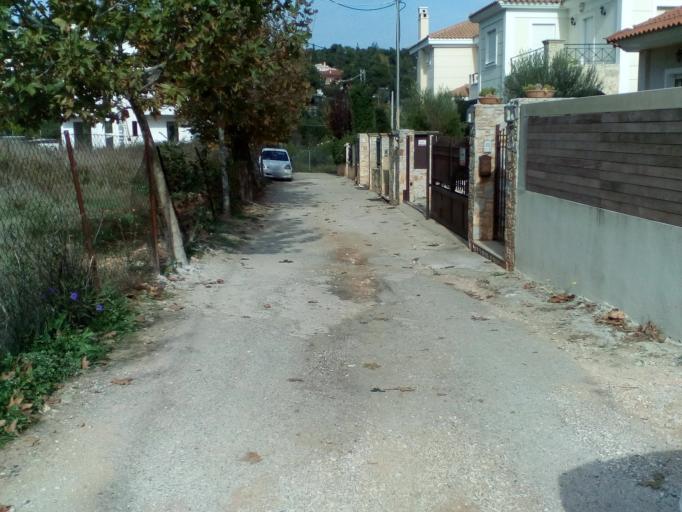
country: GR
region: Attica
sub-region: Nomarchia Anatolikis Attikis
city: Agios Stefanos
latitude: 38.1447
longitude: 23.8705
